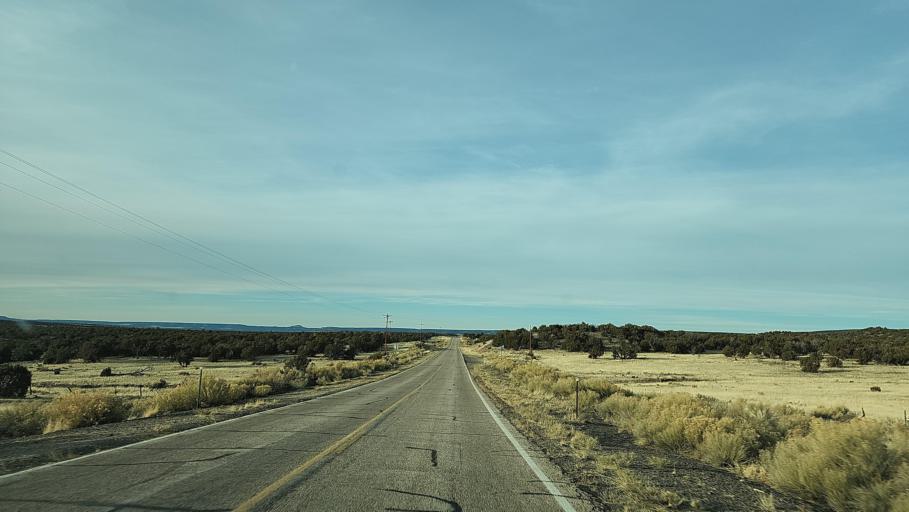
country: US
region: New Mexico
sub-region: McKinley County
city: Black Rock
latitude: 34.4297
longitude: -108.4277
